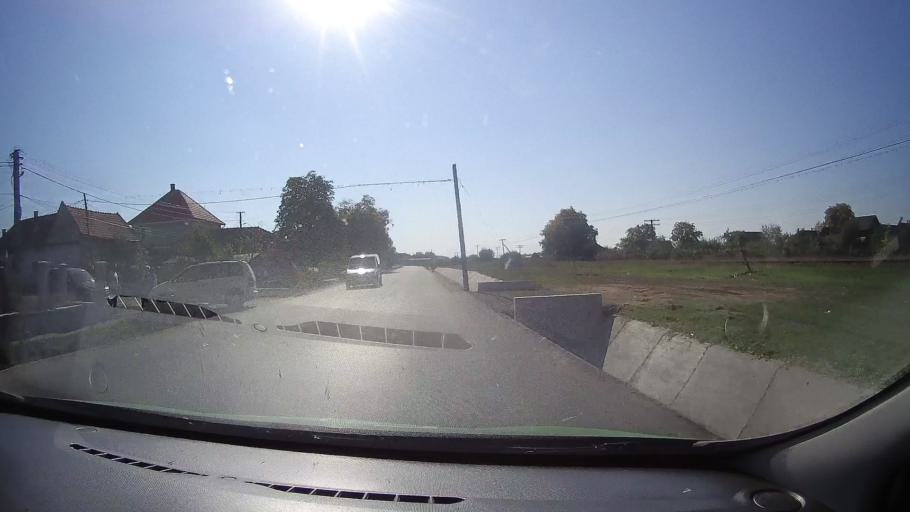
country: RO
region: Satu Mare
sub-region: Comuna Berveni
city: Lucaceni
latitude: 47.7405
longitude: 22.4747
